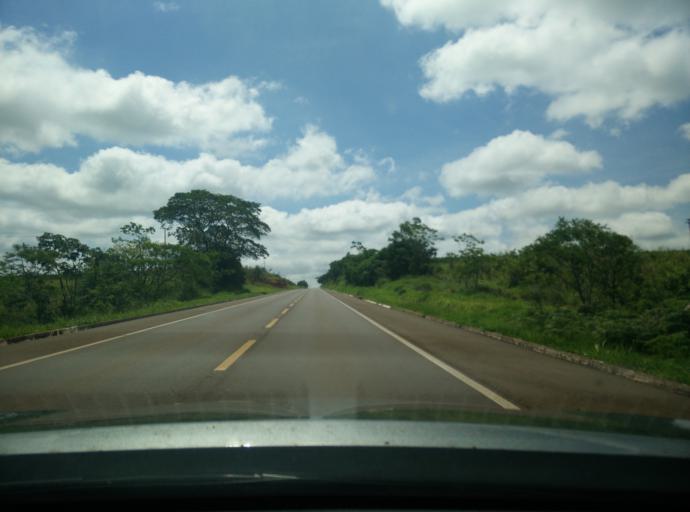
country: BR
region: Parana
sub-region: Campo Mourao
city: Campo Mourao
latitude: -23.9637
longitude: -52.5855
